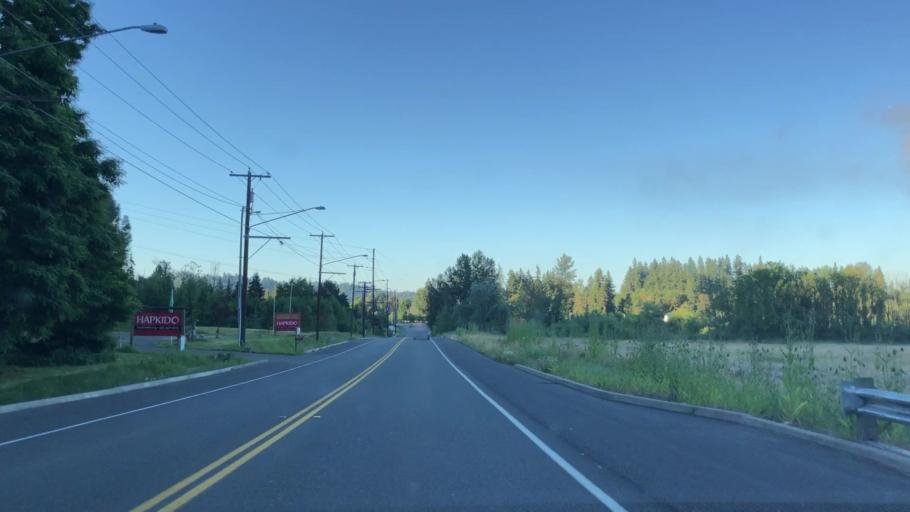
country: US
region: Washington
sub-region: King County
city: Sammamish
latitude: 47.6805
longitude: -122.0790
